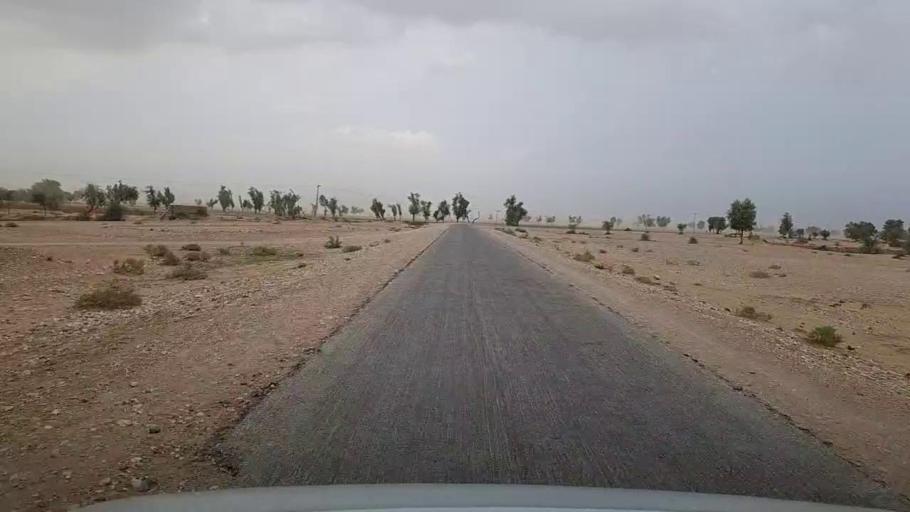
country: PK
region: Sindh
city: Sehwan
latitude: 26.3195
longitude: 67.7295
